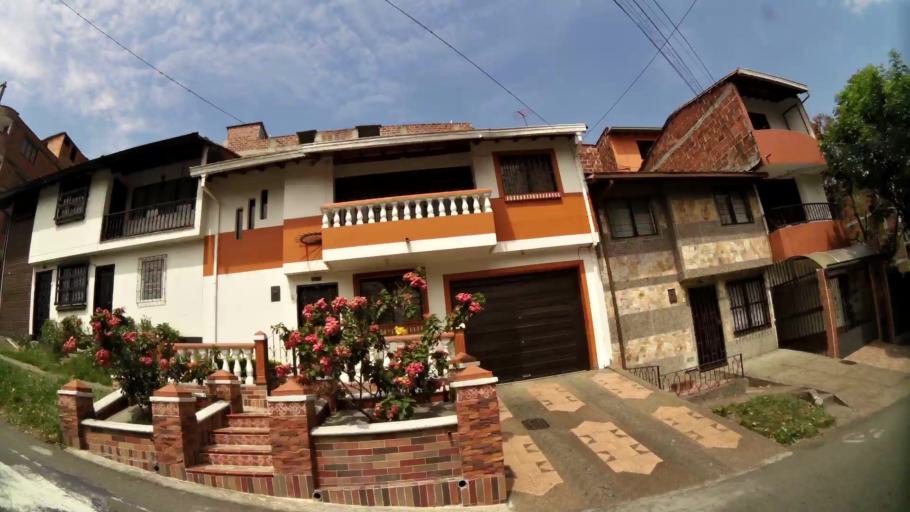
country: CO
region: Antioquia
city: Bello
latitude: 6.3147
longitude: -75.5596
